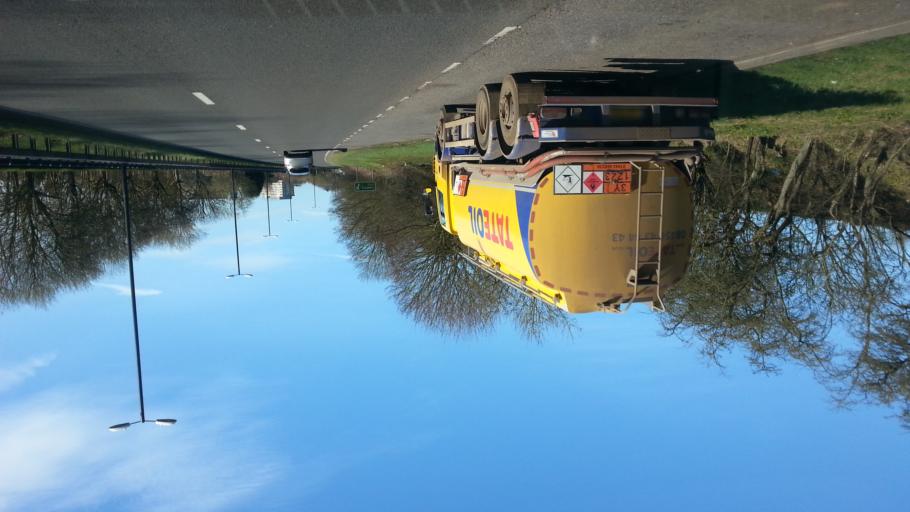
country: GB
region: England
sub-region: Coventry
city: Keresley
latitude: 52.4294
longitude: -1.5845
